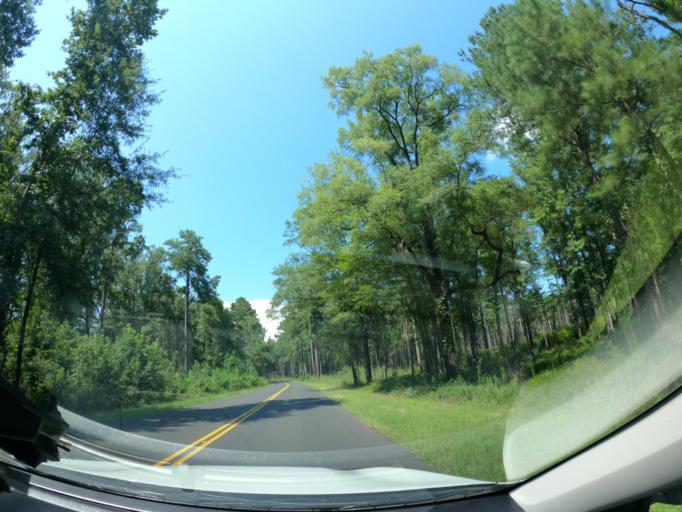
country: US
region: South Carolina
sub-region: Richland County
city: Gadsden
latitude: 33.8370
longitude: -80.8290
